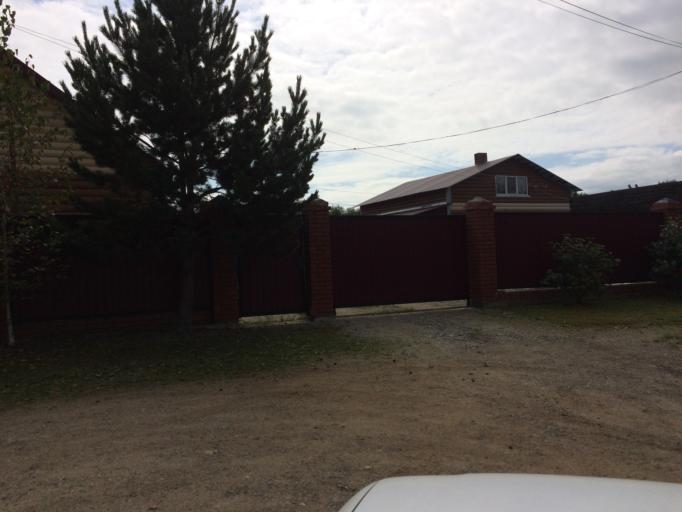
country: RU
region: Primorskiy
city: Dal'nerechensk
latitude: 45.9173
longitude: 133.7119
